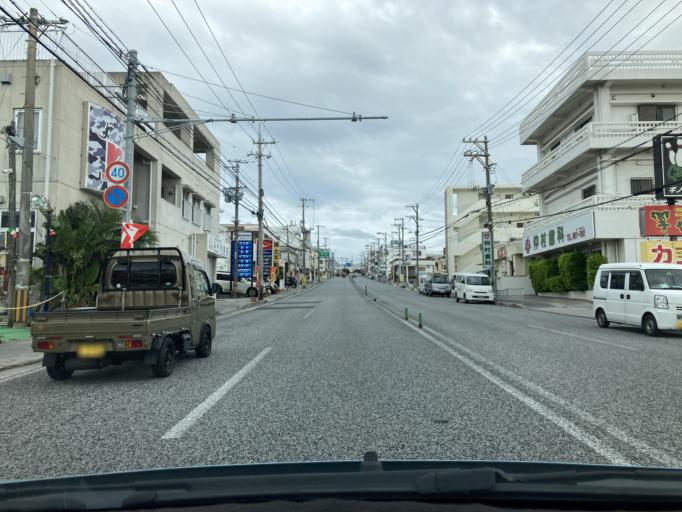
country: JP
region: Okinawa
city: Ginowan
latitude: 26.2575
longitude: 127.7504
